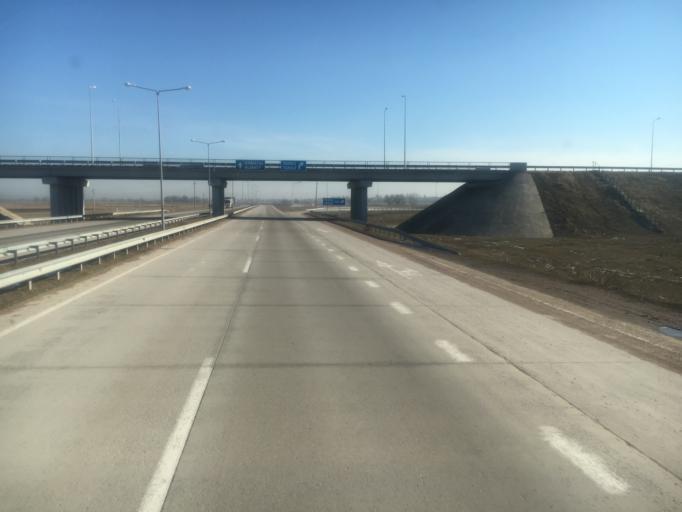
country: KZ
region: Zhambyl
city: Merke
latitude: 42.8751
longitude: 73.1361
